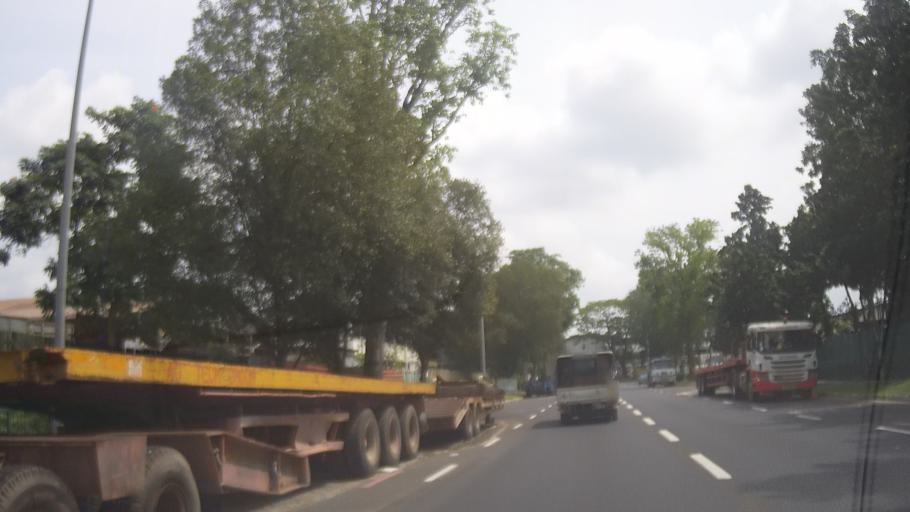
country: MY
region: Johor
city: Johor Bahru
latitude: 1.4172
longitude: 103.7496
